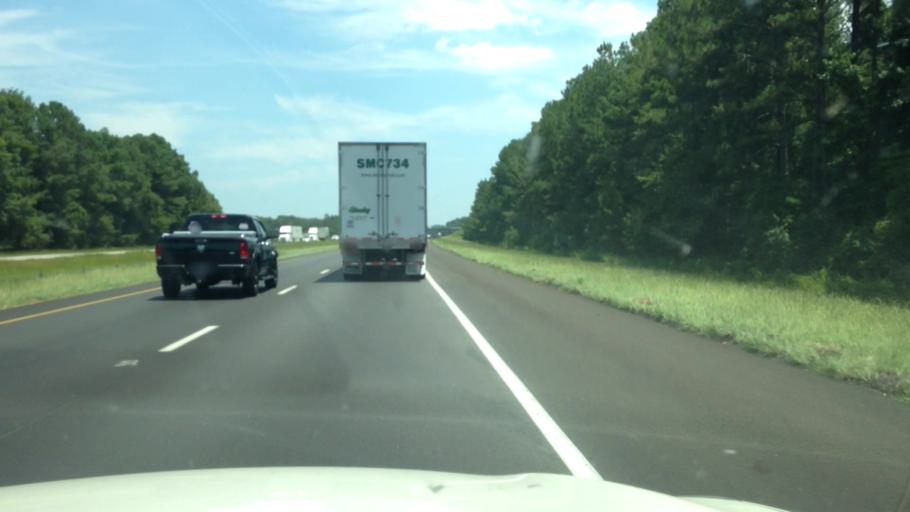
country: US
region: South Carolina
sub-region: Lee County
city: Bishopville
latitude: 34.1982
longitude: -80.0936
